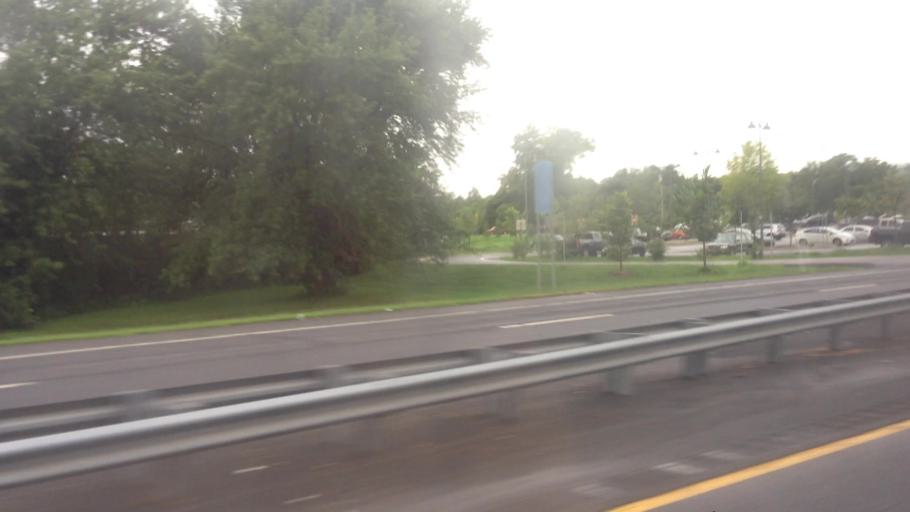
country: US
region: New York
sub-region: Ulster County
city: Kingston
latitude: 41.9427
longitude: -74.0262
